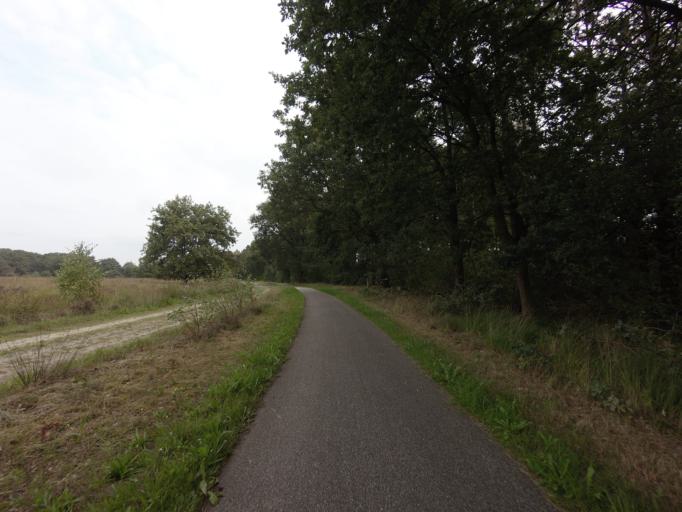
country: NL
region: Drenthe
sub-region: Gemeente Westerveld
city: Dwingeloo
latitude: 52.8981
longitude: 6.4624
